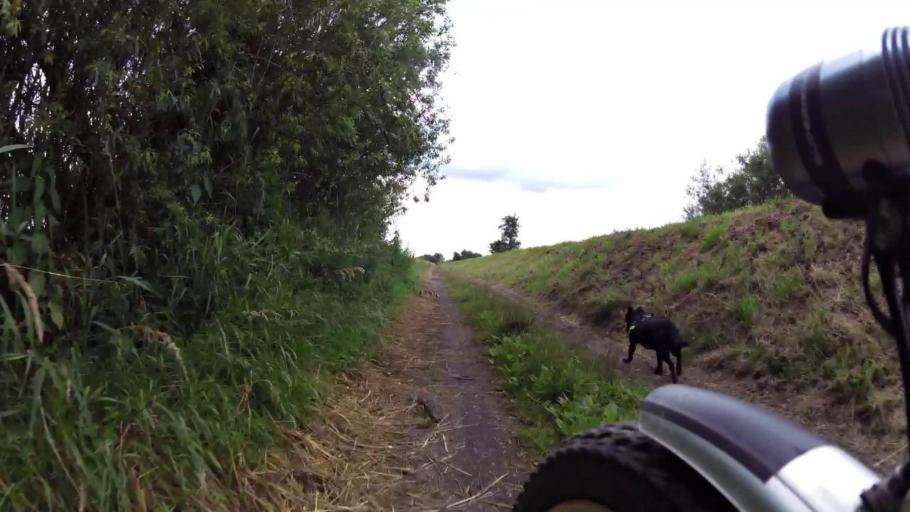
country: PL
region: West Pomeranian Voivodeship
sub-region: Powiat policki
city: Police
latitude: 53.6029
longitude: 14.5698
